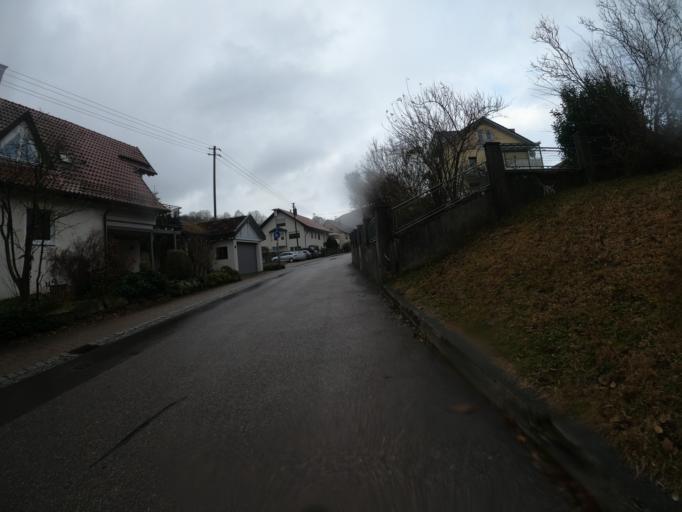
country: DE
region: Baden-Wuerttemberg
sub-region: Regierungsbezirk Stuttgart
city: Donzdorf
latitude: 48.7122
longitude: 9.8612
